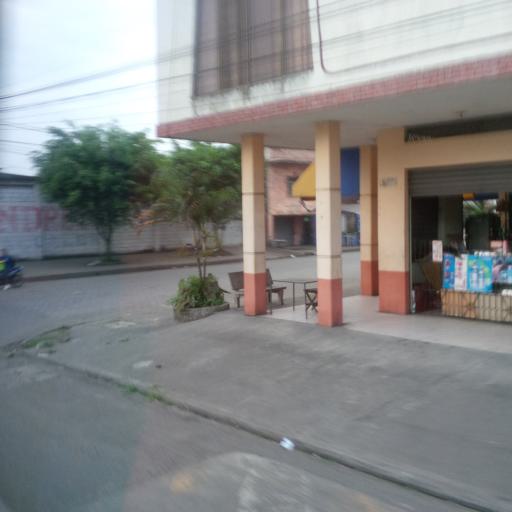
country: EC
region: Canar
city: La Troncal
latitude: -2.3304
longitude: -79.4060
